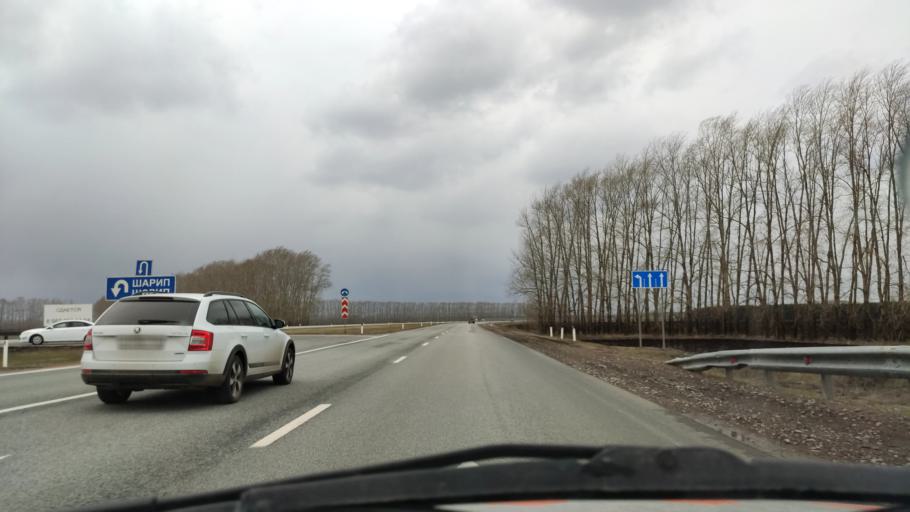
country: RU
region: Bashkortostan
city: Asanovo
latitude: 54.9819
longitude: 55.5390
